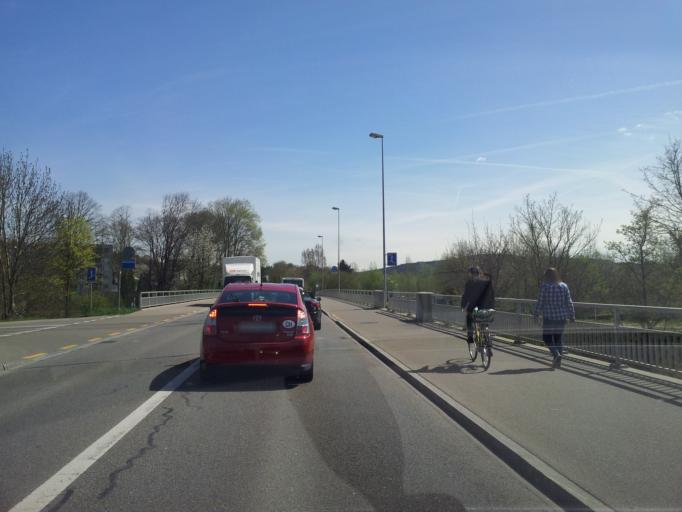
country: CH
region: Zurich
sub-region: Bezirk Dietikon
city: Dietikon / Guggenbuehl
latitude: 47.4077
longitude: 8.4086
